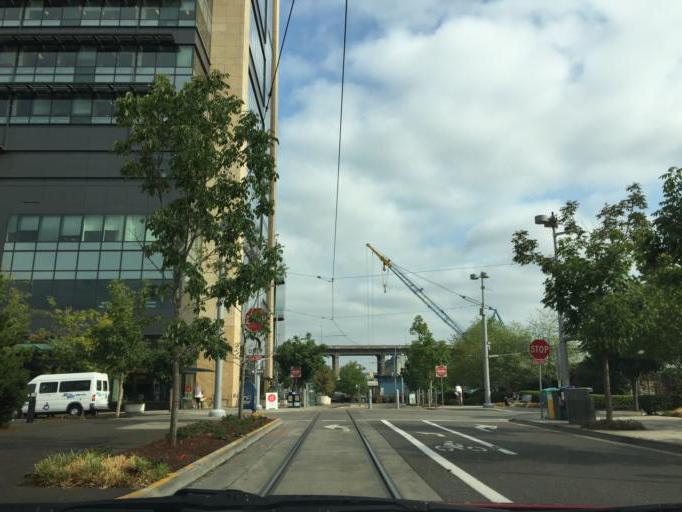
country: US
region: Oregon
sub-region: Multnomah County
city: Portland
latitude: 45.4982
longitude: -122.6708
